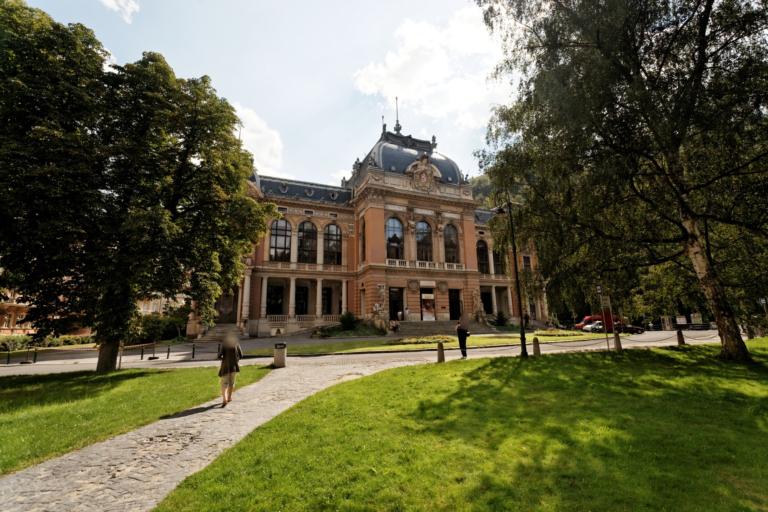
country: CZ
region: Karlovarsky
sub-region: Okres Karlovy Vary
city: Karlovy Vary
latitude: 50.2194
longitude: 12.8810
